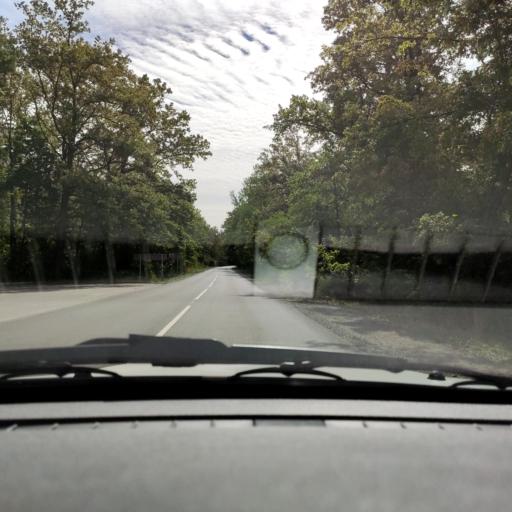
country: RU
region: Voronezj
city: Krasnolesnyy
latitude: 51.8740
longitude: 39.6527
